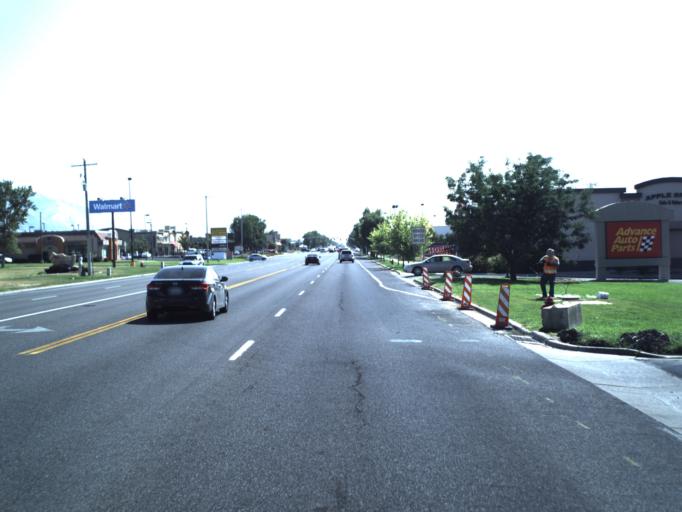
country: US
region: Utah
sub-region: Cache County
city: Logan
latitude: 41.7614
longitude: -111.8344
